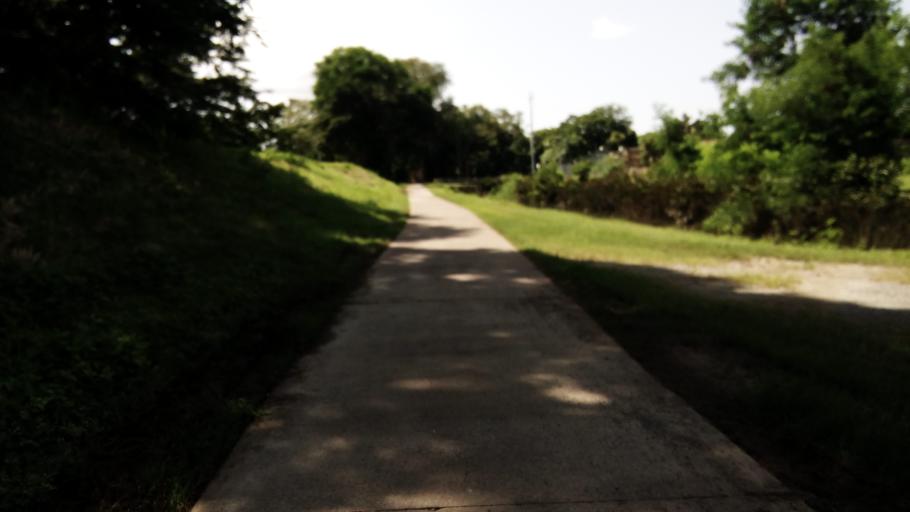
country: AU
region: Queensland
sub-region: Cairns
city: Cairns
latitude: -16.9129
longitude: 145.7607
